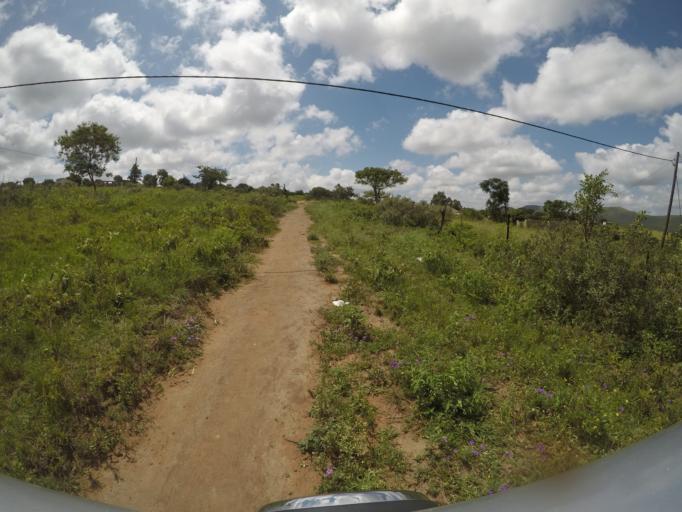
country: ZA
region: KwaZulu-Natal
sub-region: uThungulu District Municipality
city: Empangeni
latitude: -28.5821
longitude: 31.8408
